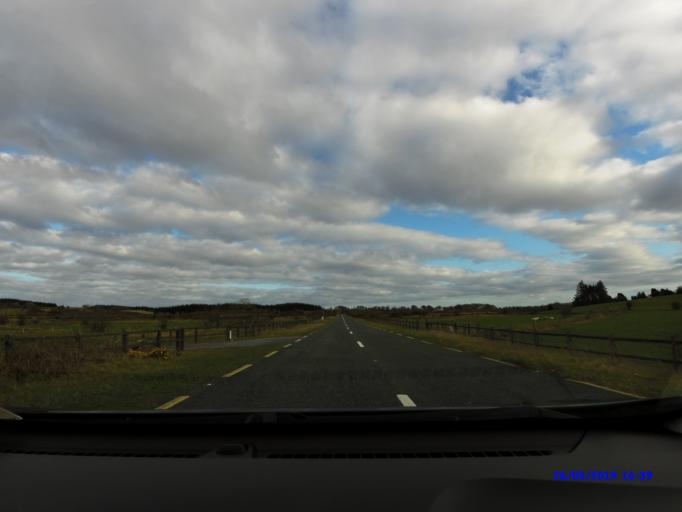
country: IE
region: Connaught
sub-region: Maigh Eo
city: Ballyhaunis
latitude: 53.8827
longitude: -8.7920
